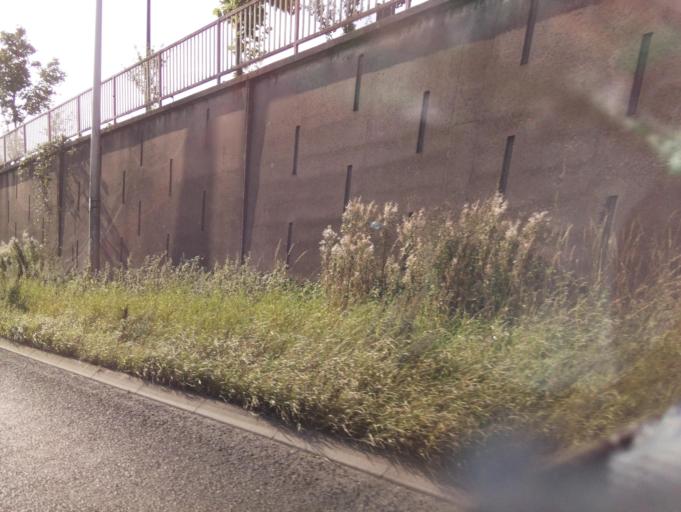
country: GB
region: England
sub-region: Sandwell
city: West Bromwich
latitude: 52.5209
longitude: -1.9882
